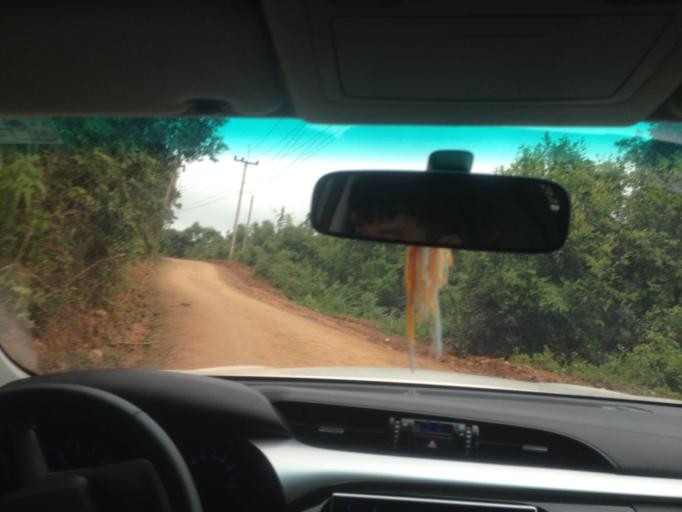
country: TH
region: Nan
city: Chaloem Phra Kiat
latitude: 19.9686
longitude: 101.1369
